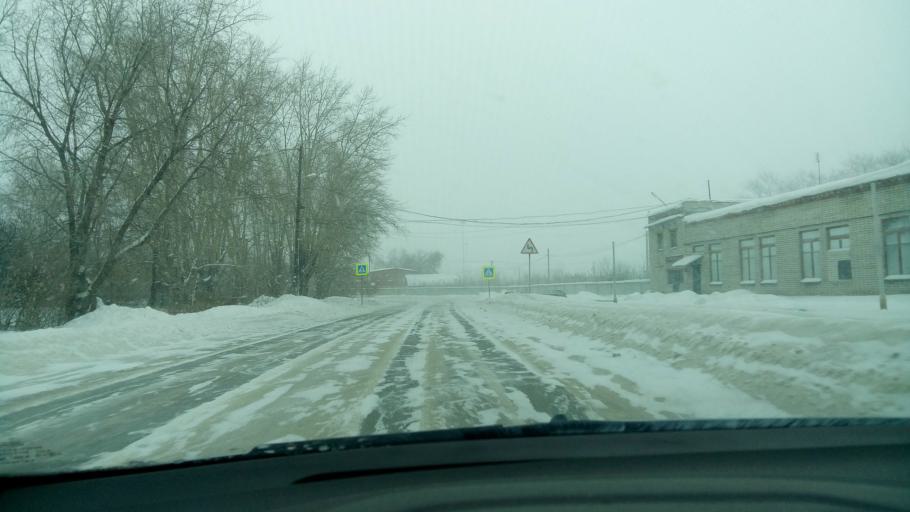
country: RU
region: Sverdlovsk
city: Bogdanovich
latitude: 56.7809
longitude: 62.0398
